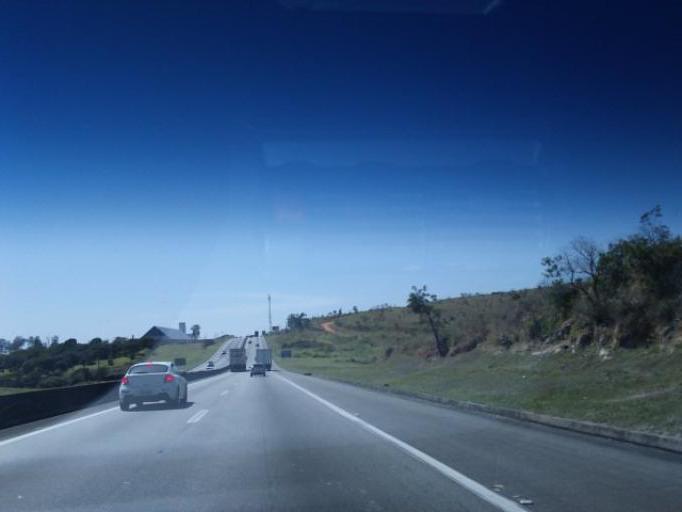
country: BR
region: Sao Paulo
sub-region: Cacapava
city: Cacapava
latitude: -23.0689
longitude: -45.6393
